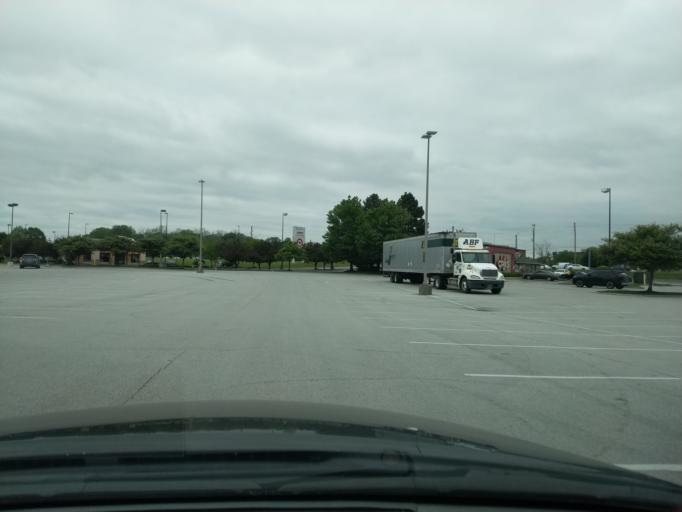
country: US
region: Indiana
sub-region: Marion County
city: Speedway
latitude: 39.8220
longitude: -86.2802
